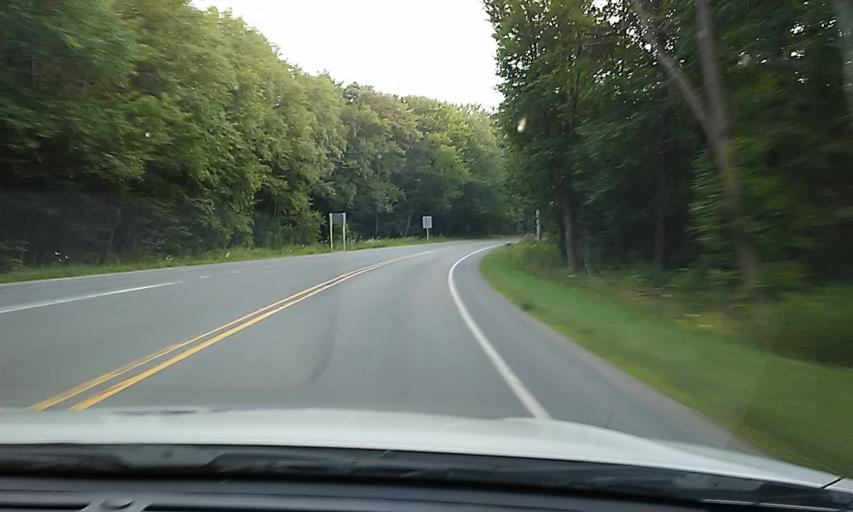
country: US
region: Pennsylvania
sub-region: McKean County
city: Kane
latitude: 41.6198
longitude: -78.8287
